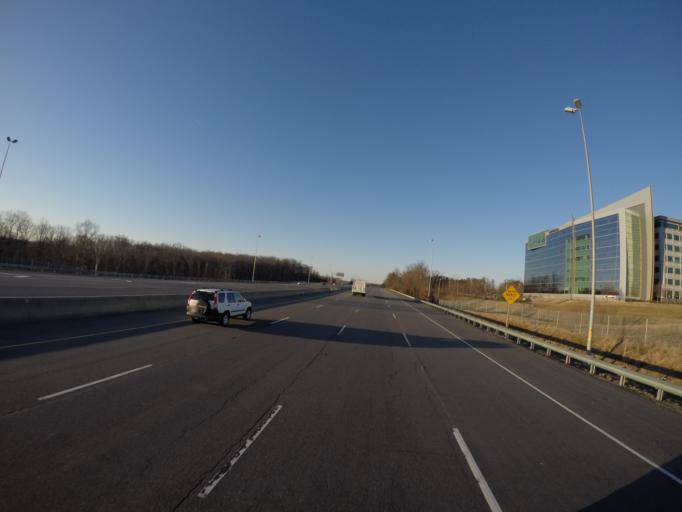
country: US
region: Virginia
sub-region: Loudoun County
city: Dulles Town Center
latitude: 39.0340
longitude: -77.4312
